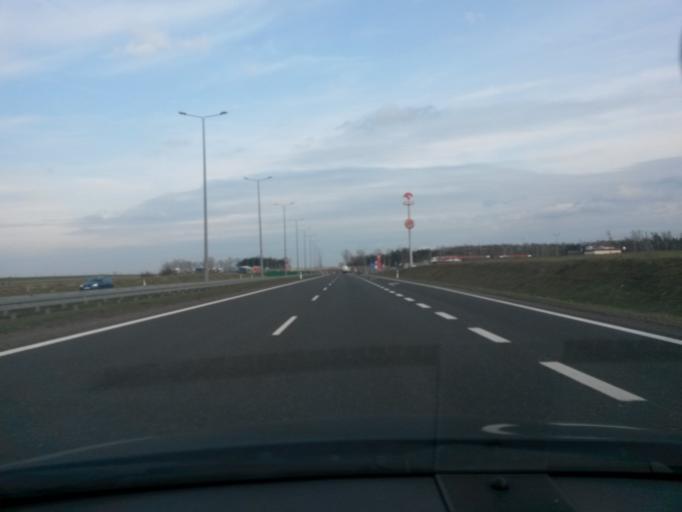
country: PL
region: Lodz Voivodeship
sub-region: Powiat zgierski
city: Parzeczew
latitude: 51.9463
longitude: 19.1724
